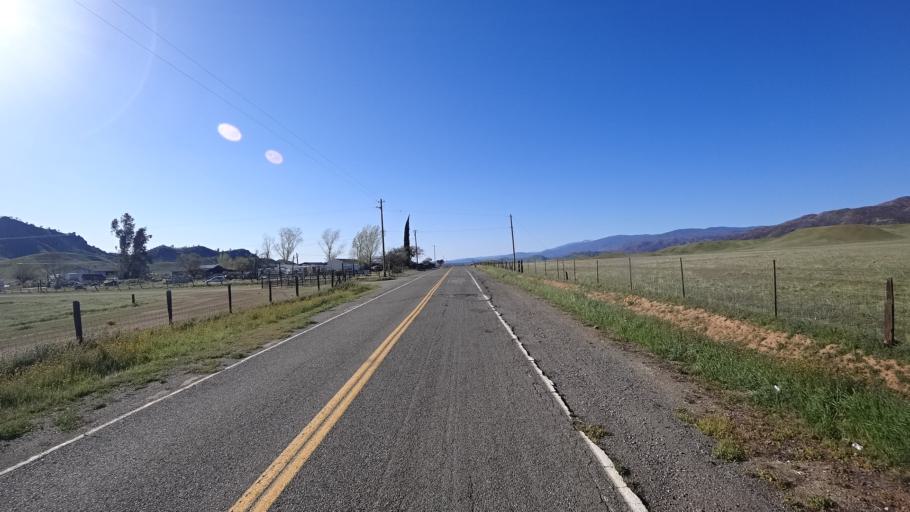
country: US
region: California
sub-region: Tehama County
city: Rancho Tehama Reserve
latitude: 39.7277
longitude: -122.5496
